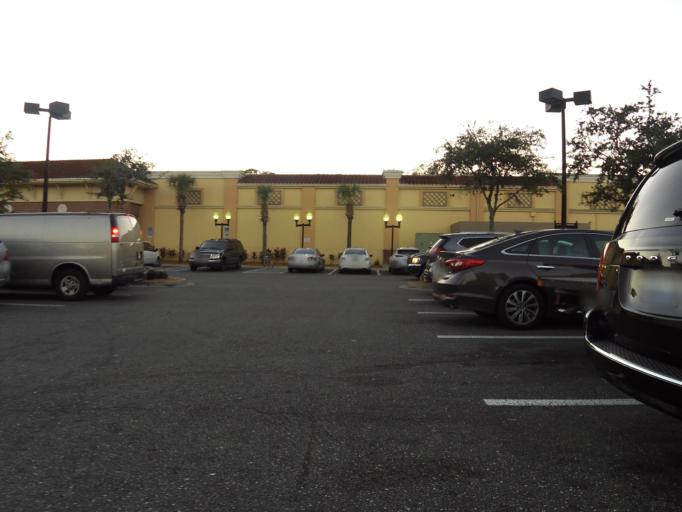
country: US
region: Florida
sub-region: Duval County
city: Jacksonville
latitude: 30.3116
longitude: -81.6816
